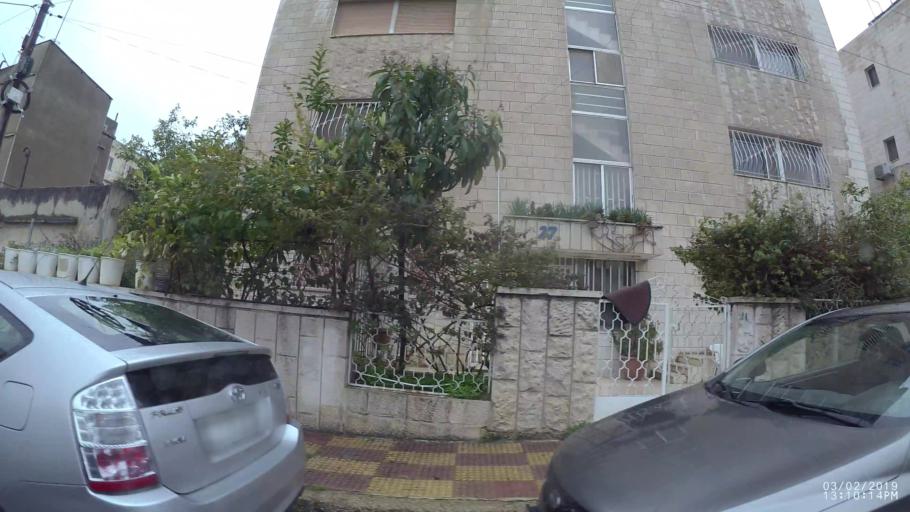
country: JO
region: Amman
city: Amman
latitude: 31.9580
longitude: 35.9241
